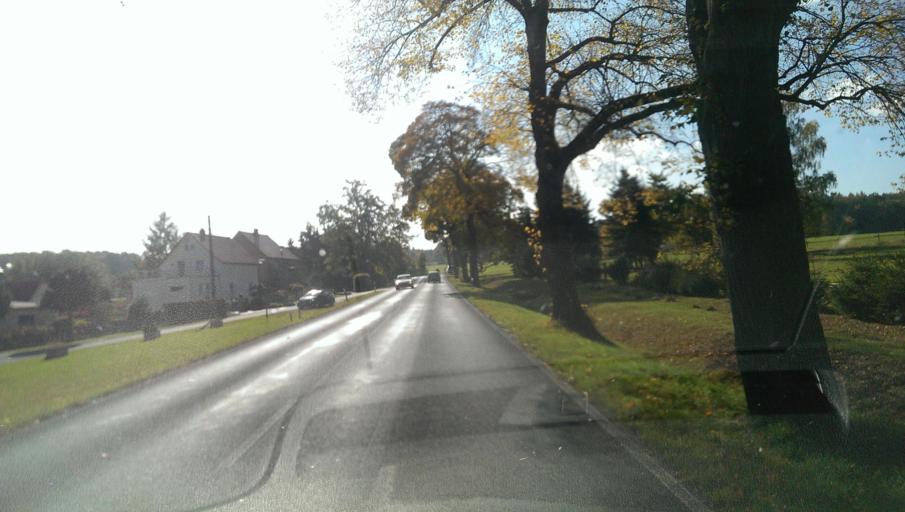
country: DE
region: Saxony
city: Dohma
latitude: 50.8977
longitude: 13.9459
